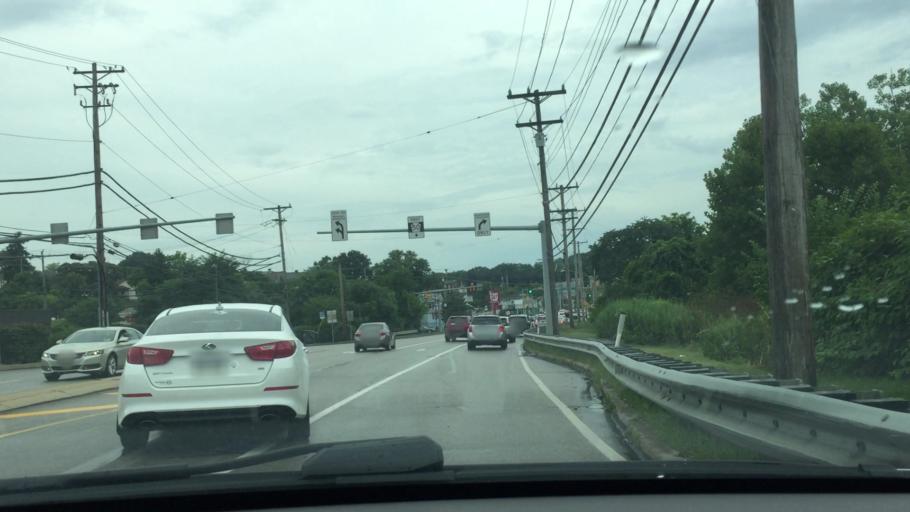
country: US
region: Pennsylvania
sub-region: Allegheny County
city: Heidelberg
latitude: 40.3868
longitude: -80.0921
